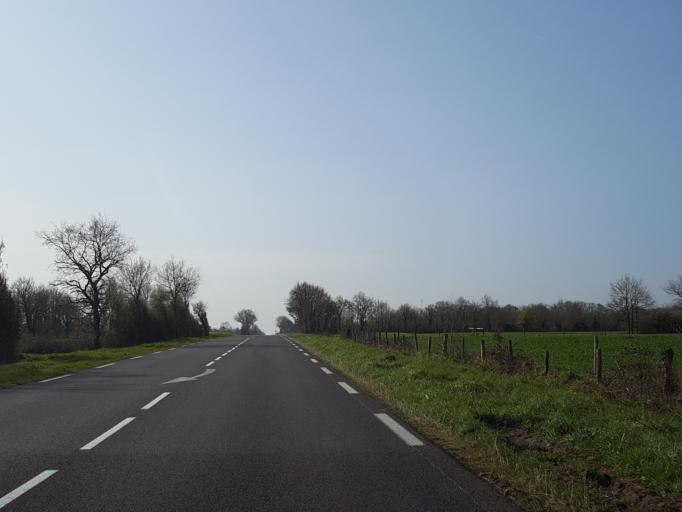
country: FR
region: Pays de la Loire
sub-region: Departement de la Vendee
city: Les Lucs-sur-Boulogne
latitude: 46.8855
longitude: -1.5011
